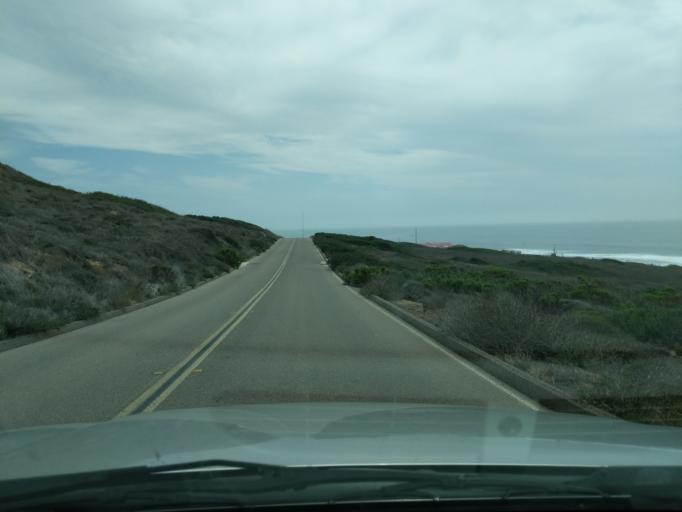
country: US
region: California
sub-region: San Diego County
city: Coronado
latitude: 32.6702
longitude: -117.2437
